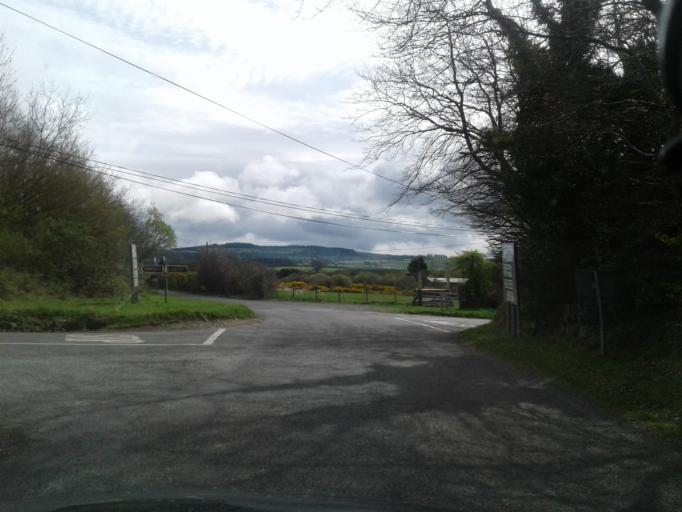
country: IE
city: Newtownmountkennedy
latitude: 53.0903
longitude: -6.2212
